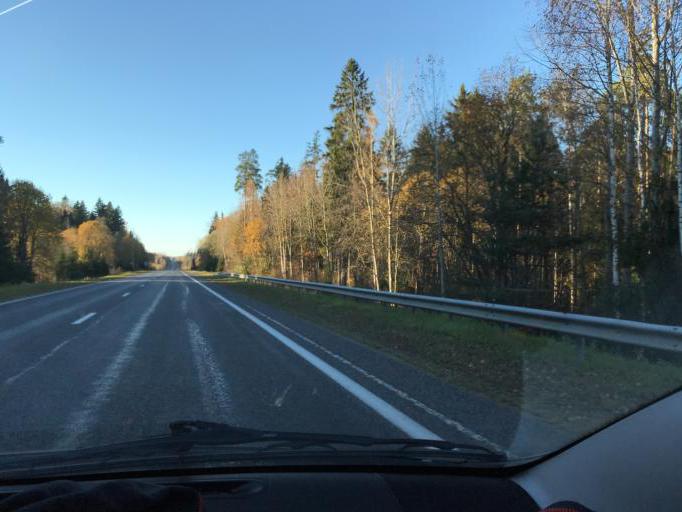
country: BY
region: Vitebsk
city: Vitebsk
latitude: 55.3413
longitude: 30.2323
